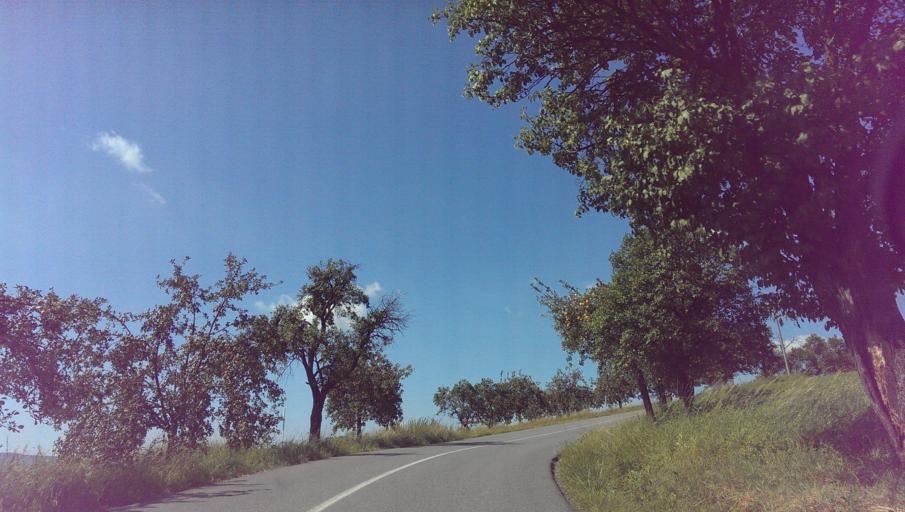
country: CZ
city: Hukvaldy
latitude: 49.6262
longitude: 18.1999
